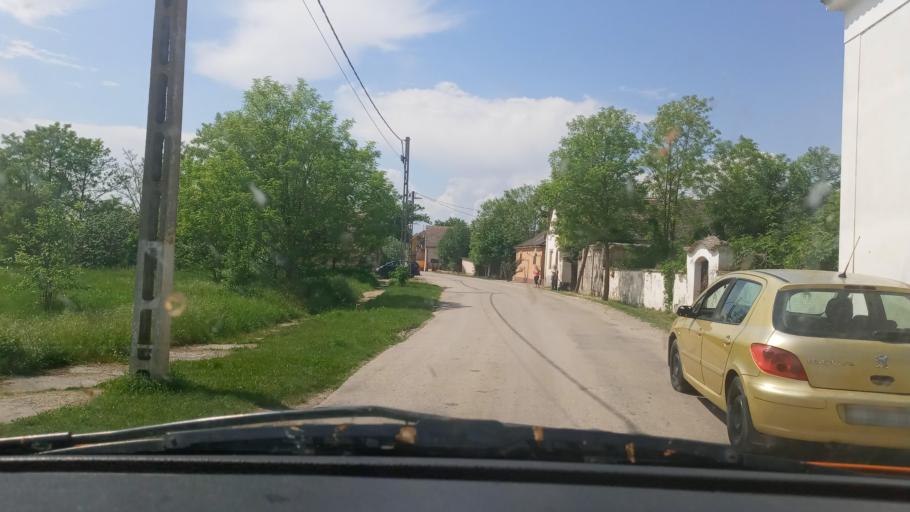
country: HU
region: Baranya
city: Beremend
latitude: 45.8228
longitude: 18.3662
